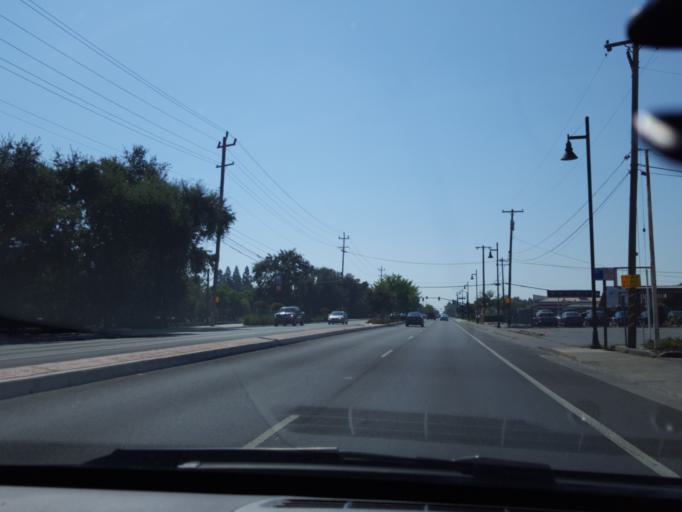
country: US
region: California
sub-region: Sacramento County
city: Rancho Cordova
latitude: 38.5843
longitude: -121.3130
